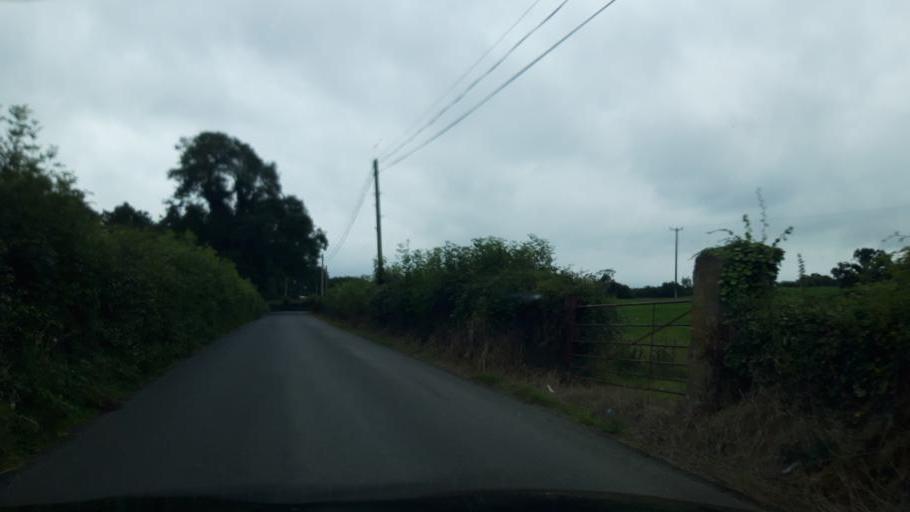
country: IE
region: Leinster
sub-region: Kilkenny
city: Ballyragget
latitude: 52.7153
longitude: -7.4026
